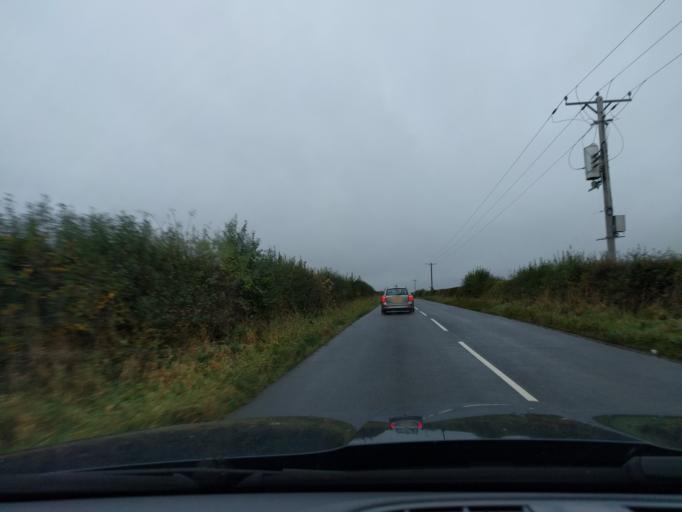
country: GB
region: England
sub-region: Northumberland
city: Ford
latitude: 55.7324
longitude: -2.1015
